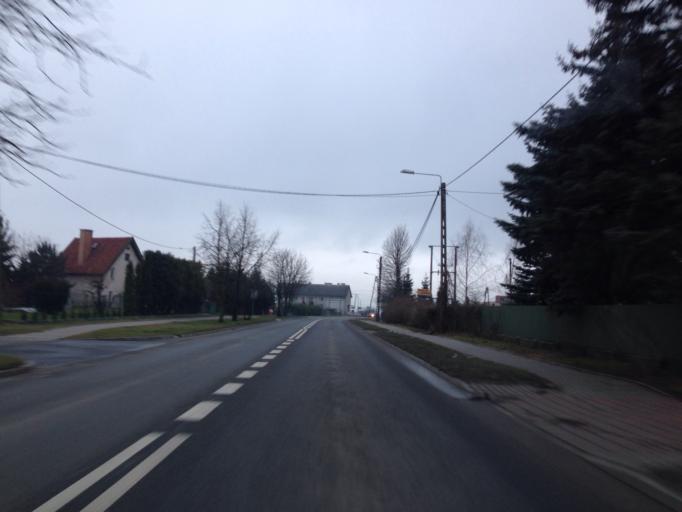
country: PL
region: Warmian-Masurian Voivodeship
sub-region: Powiat ketrzynski
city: Ketrzyn
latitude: 54.0693
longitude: 21.3695
